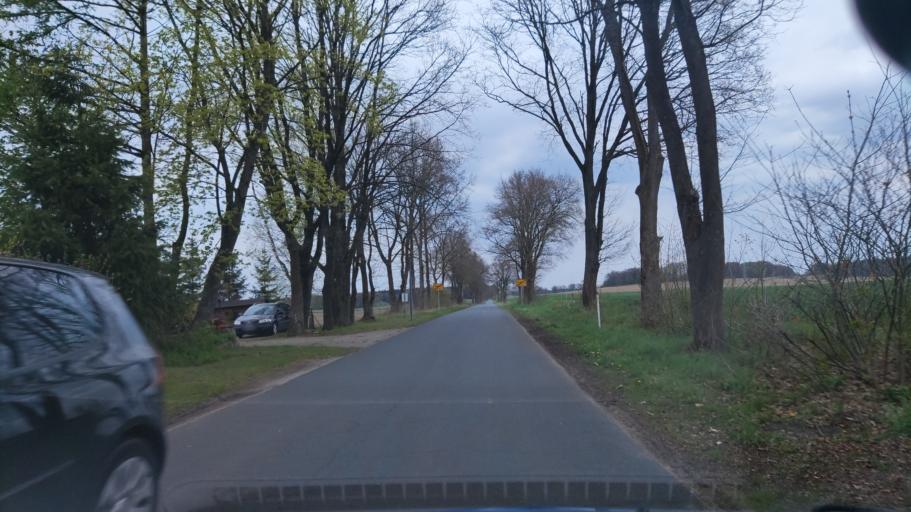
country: DE
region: Lower Saxony
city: Oldendorf
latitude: 53.1568
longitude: 10.2227
